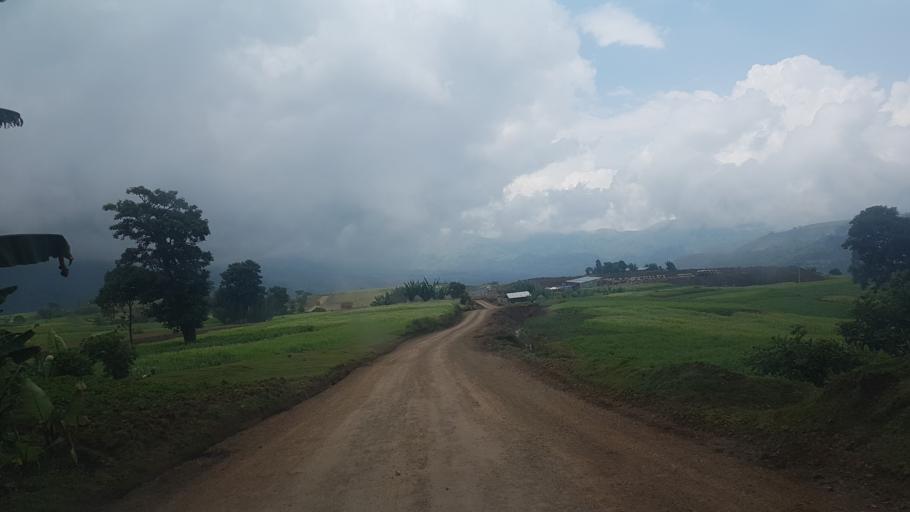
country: ET
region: Southern Nations, Nationalities, and People's Region
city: Arba Minch'
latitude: 6.3262
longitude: 37.5451
